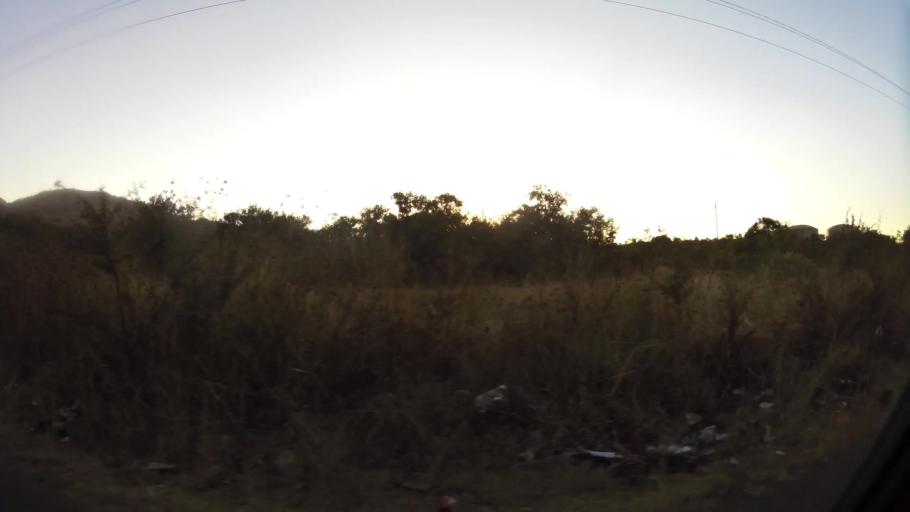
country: ZA
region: North-West
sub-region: Bojanala Platinum District Municipality
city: Rustenburg
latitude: -25.6353
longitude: 27.2015
